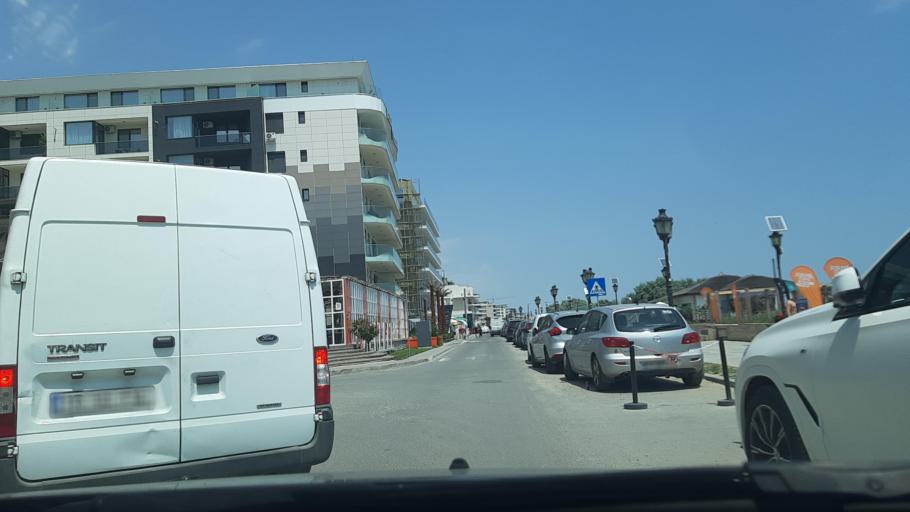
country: RO
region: Constanta
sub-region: Comuna Navodari
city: Navodari
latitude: 44.2980
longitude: 28.6254
